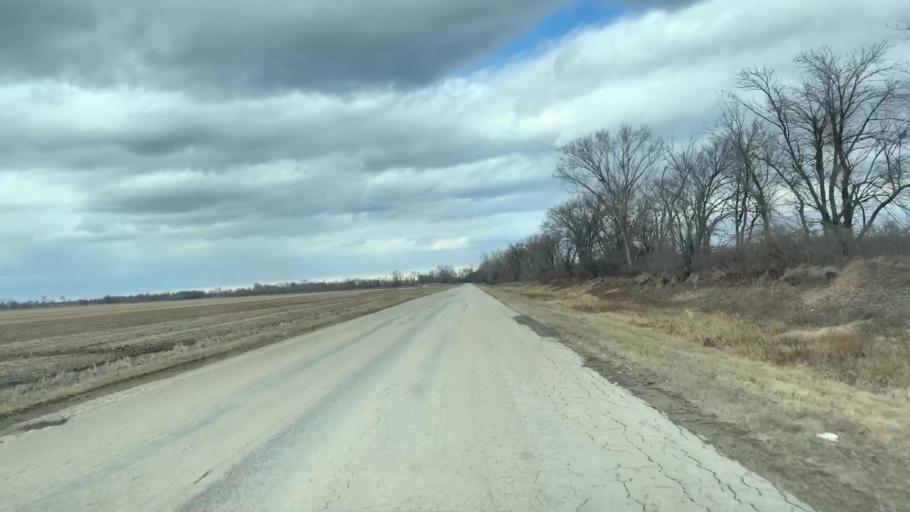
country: US
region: Kansas
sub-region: Allen County
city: Humboldt
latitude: 37.7934
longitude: -95.4706
